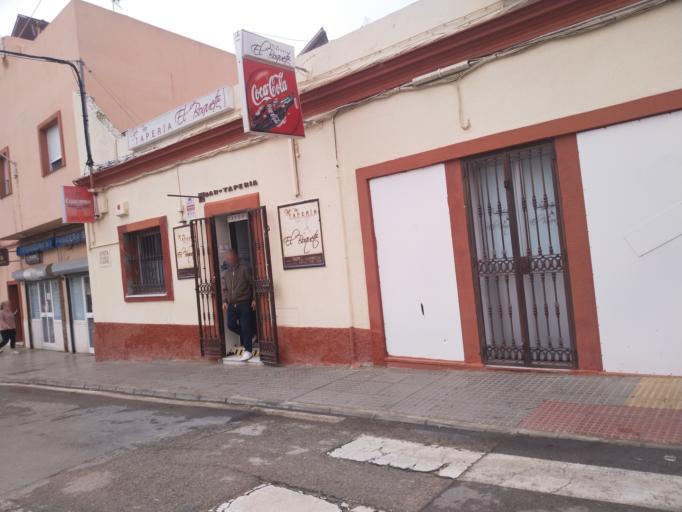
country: ES
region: Andalusia
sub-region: Provincia de Cadiz
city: San Fernando
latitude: 36.4783
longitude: -6.1965
